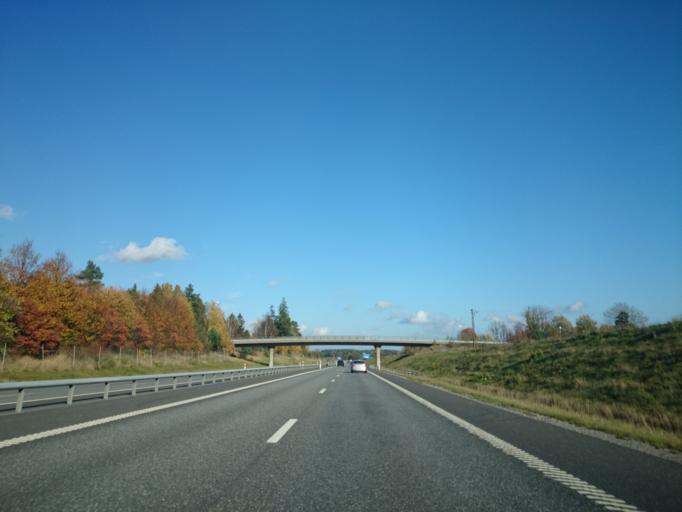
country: SE
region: Stockholm
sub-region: Haninge Kommun
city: Jordbro
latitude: 59.0945
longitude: 18.1023
